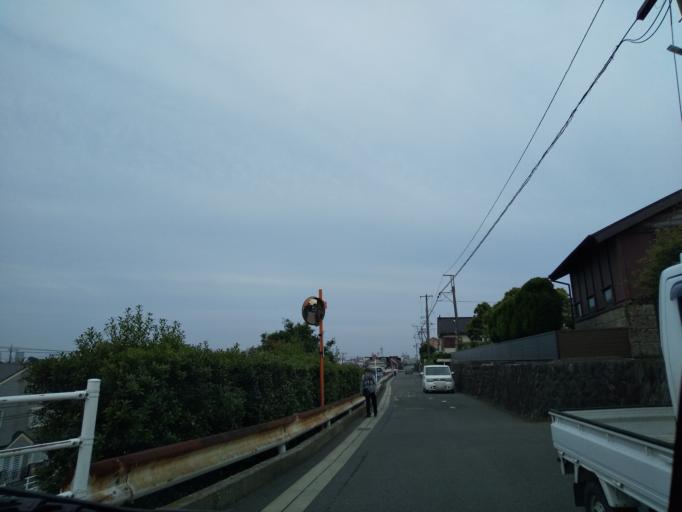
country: JP
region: Kanagawa
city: Atsugi
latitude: 35.4700
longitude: 139.3539
